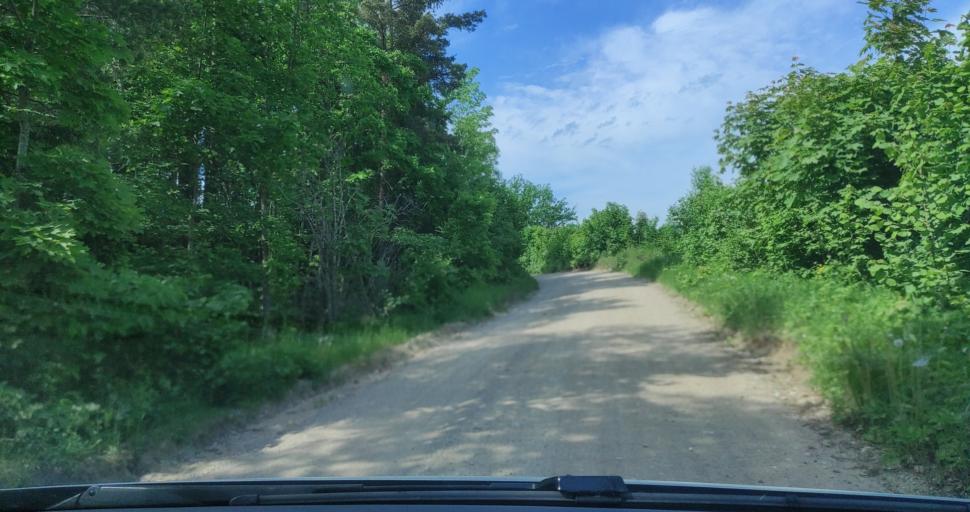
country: LV
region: Kuldigas Rajons
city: Kuldiga
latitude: 56.8542
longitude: 21.9112
